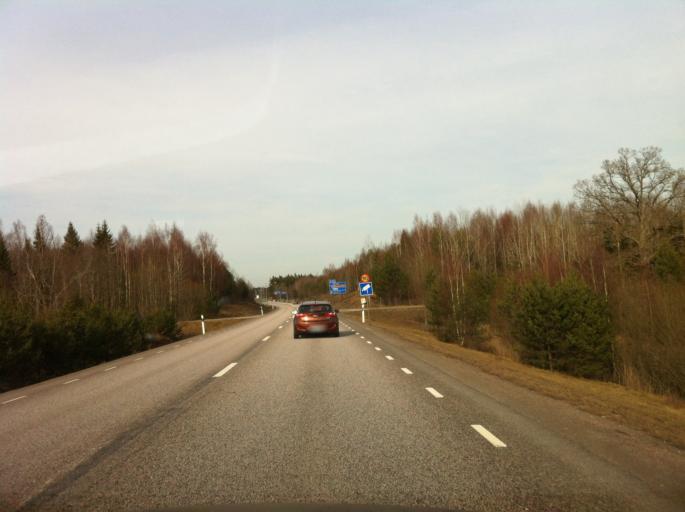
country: SE
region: Vaestra Goetaland
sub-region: Toreboda Kommun
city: Toereboda
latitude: 58.8263
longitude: 13.9884
